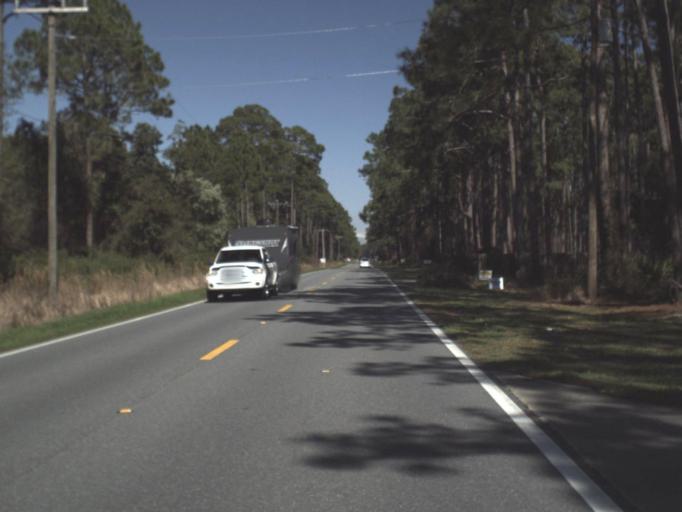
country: US
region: Florida
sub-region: Franklin County
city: Carrabelle
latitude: 29.8929
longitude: -84.5682
